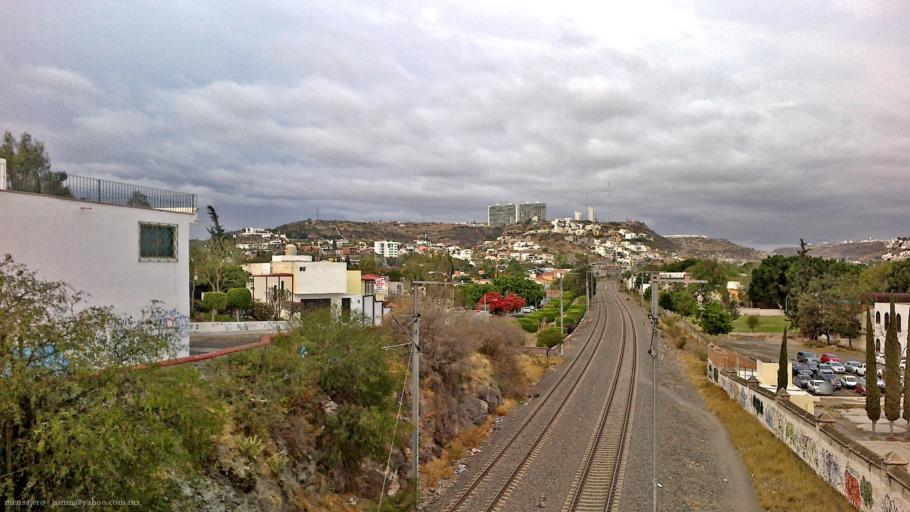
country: MX
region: Queretaro
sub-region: Queretaro
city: Santiago de Queretaro
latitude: 20.6023
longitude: -100.3866
